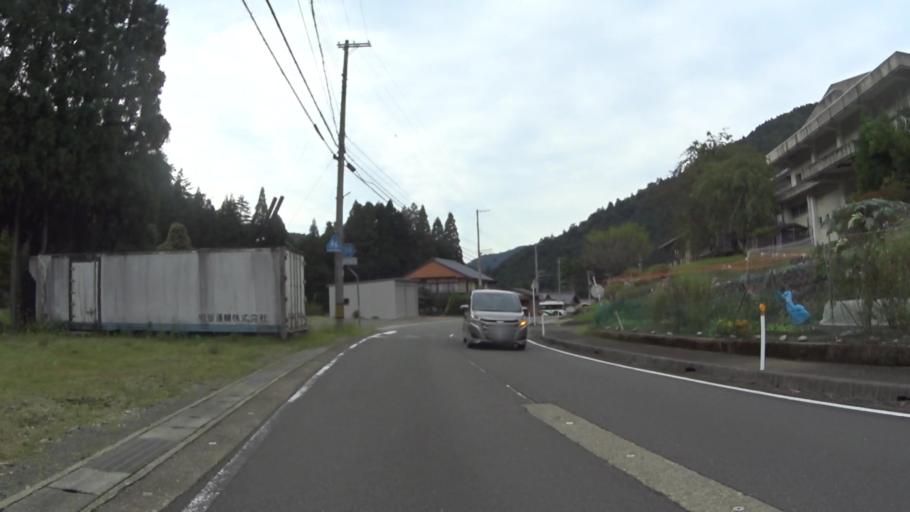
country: JP
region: Fukui
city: Obama
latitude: 35.3133
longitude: 135.6451
